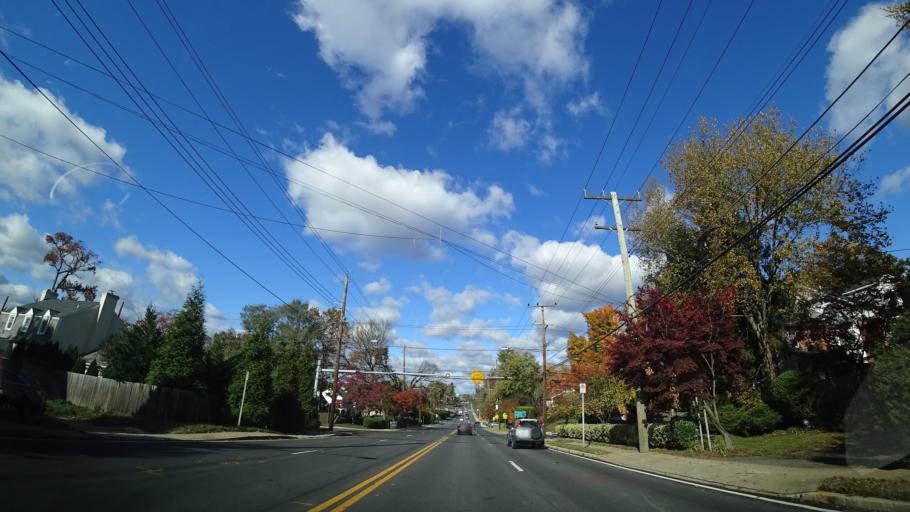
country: US
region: Maryland
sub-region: Montgomery County
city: Friendship Village
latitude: 38.9592
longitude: -77.0951
